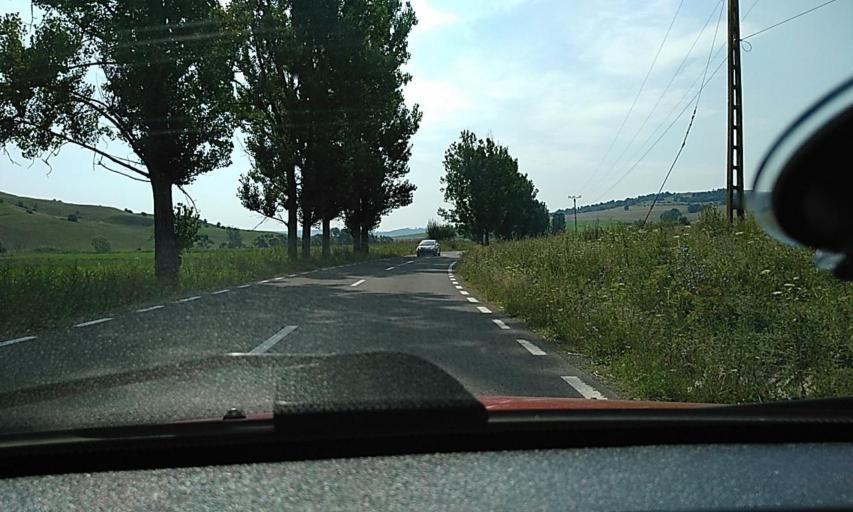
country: RO
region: Brasov
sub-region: Oras Rupea
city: Fiser
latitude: 46.0474
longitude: 25.1160
